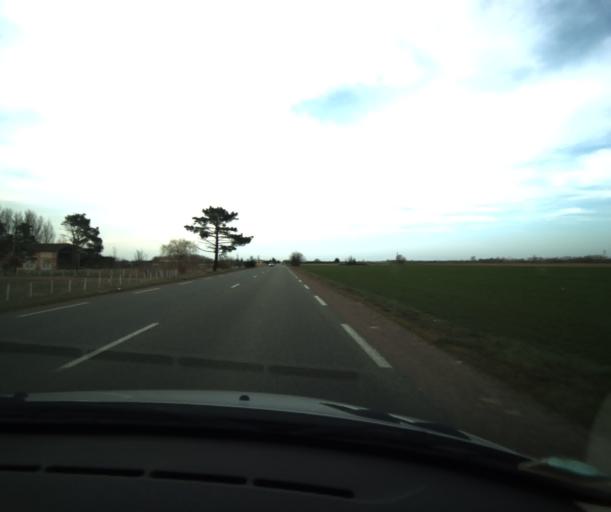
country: FR
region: Midi-Pyrenees
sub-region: Departement du Tarn-et-Garonne
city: Montech
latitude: 43.9668
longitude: 1.2076
